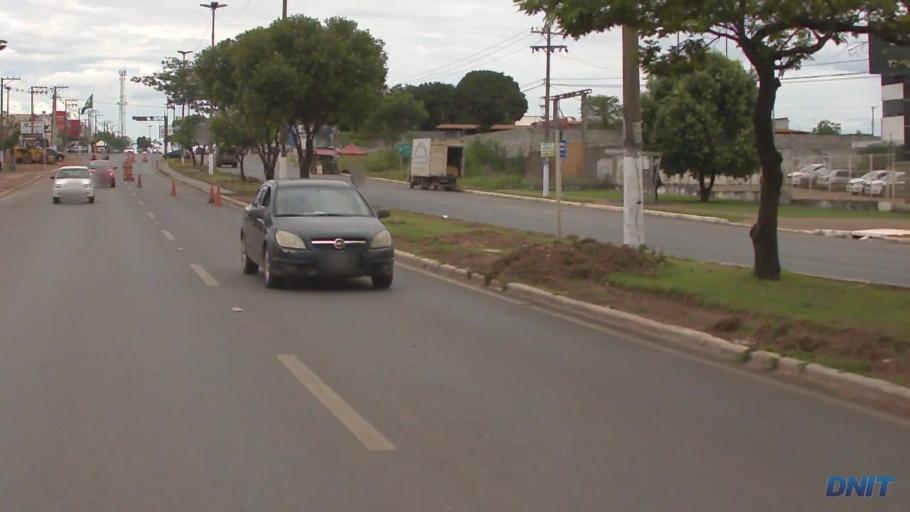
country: BR
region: Mato Grosso
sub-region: Varzea Grande
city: Varzea Grande
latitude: -15.6421
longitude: -56.1639
